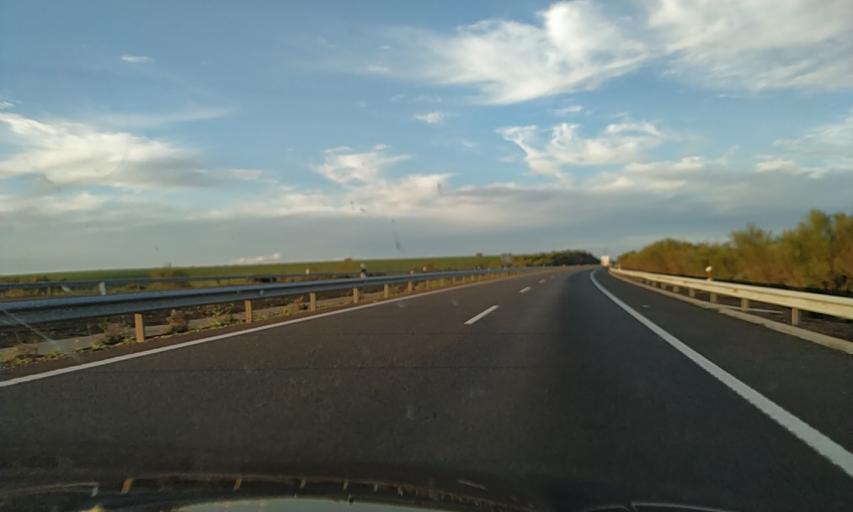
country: ES
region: Extremadura
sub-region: Provincia de Badajoz
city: Merida
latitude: 38.9612
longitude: -6.3420
